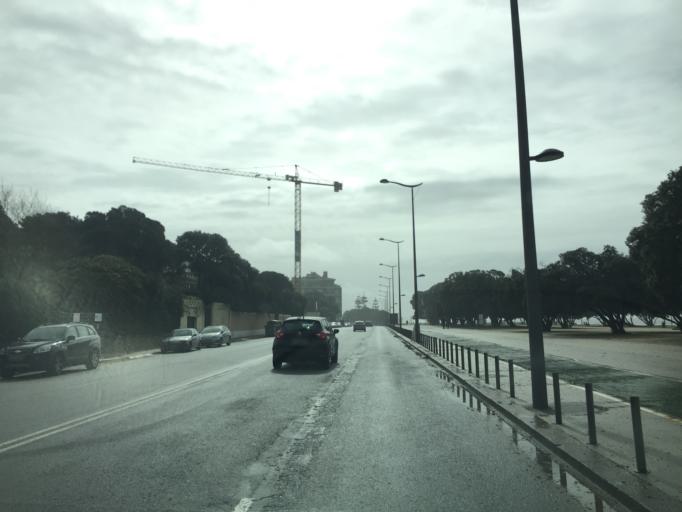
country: PT
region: Porto
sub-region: Matosinhos
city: Matosinhos
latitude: 41.1616
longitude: -8.6850
